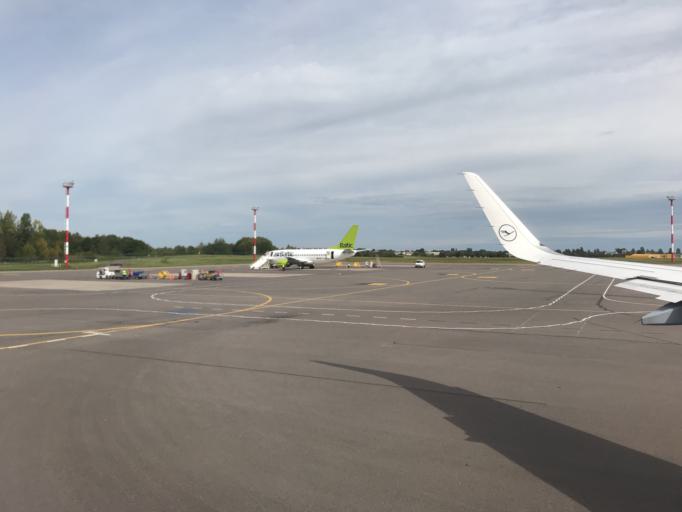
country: LT
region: Vilnius County
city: Naujamiestis
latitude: 54.6445
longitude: 25.2828
